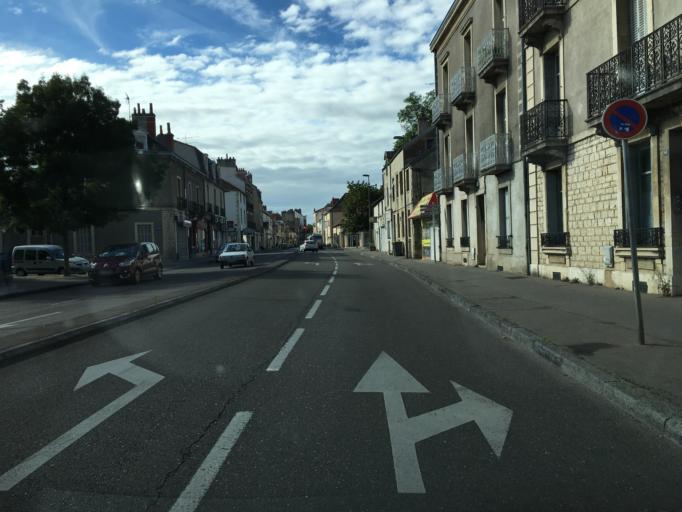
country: FR
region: Bourgogne
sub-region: Departement de la Cote-d'Or
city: Longvic
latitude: 47.3136
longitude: 5.0498
